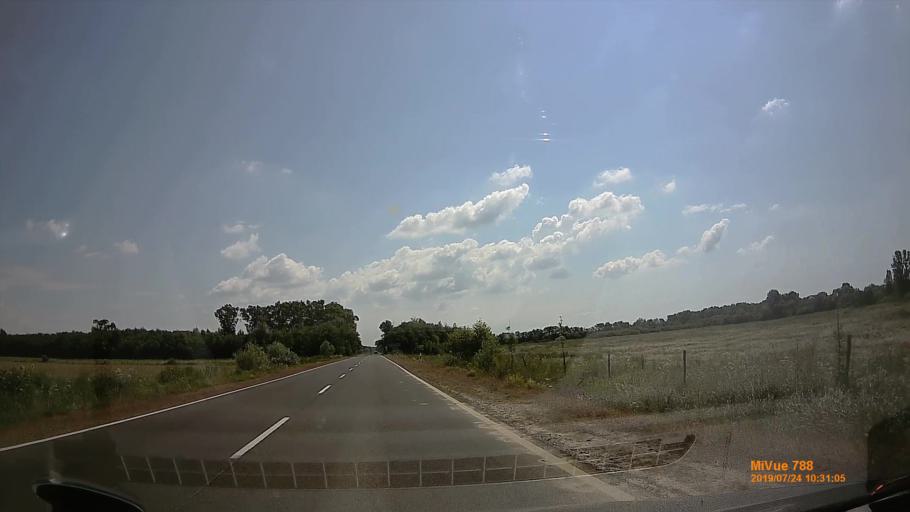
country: HU
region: Szabolcs-Szatmar-Bereg
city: Tarpa
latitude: 48.1605
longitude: 22.5042
